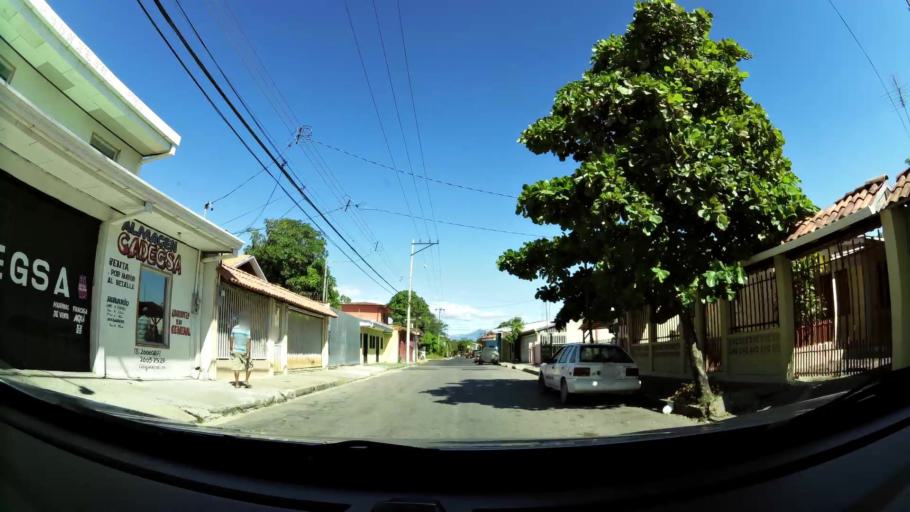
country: CR
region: Guanacaste
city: Liberia
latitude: 10.6329
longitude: -85.4342
